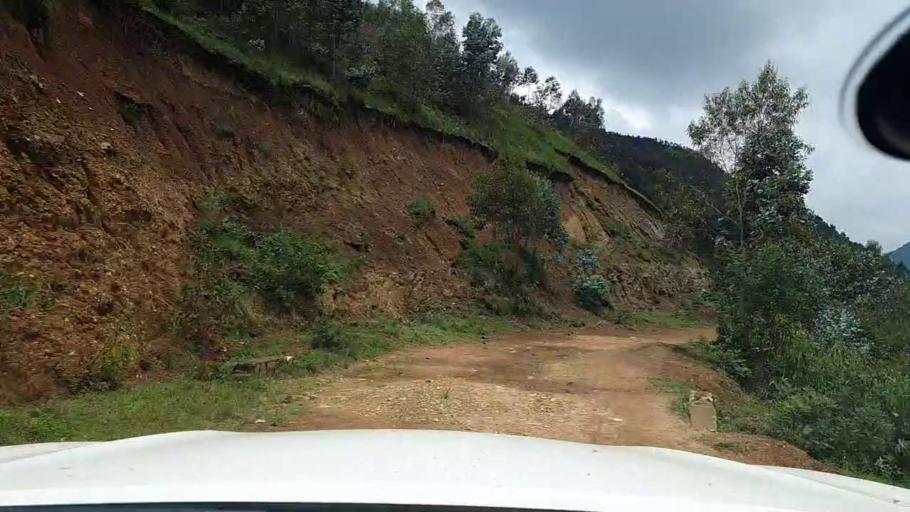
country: RW
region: Western Province
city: Kibuye
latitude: -2.1527
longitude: 29.4527
